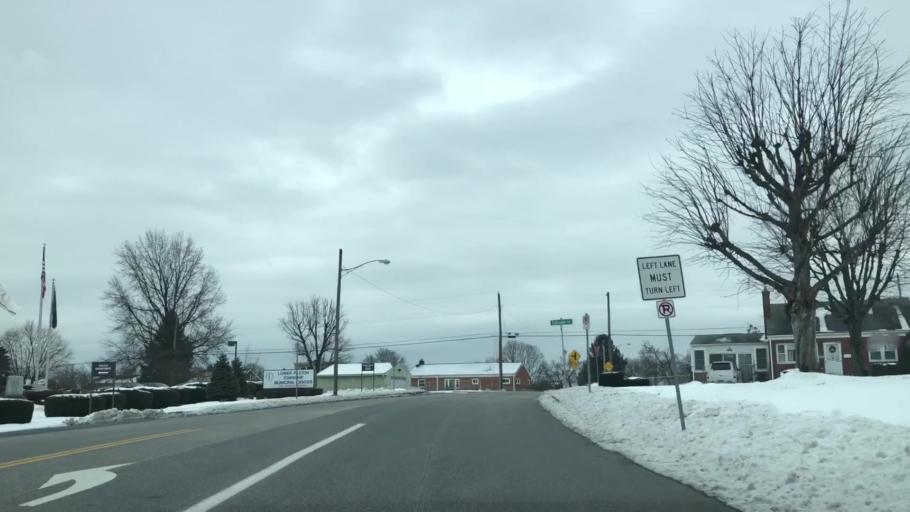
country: US
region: Pennsylvania
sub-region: Dauphin County
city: Colonial Park
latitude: 40.2980
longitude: -76.8067
